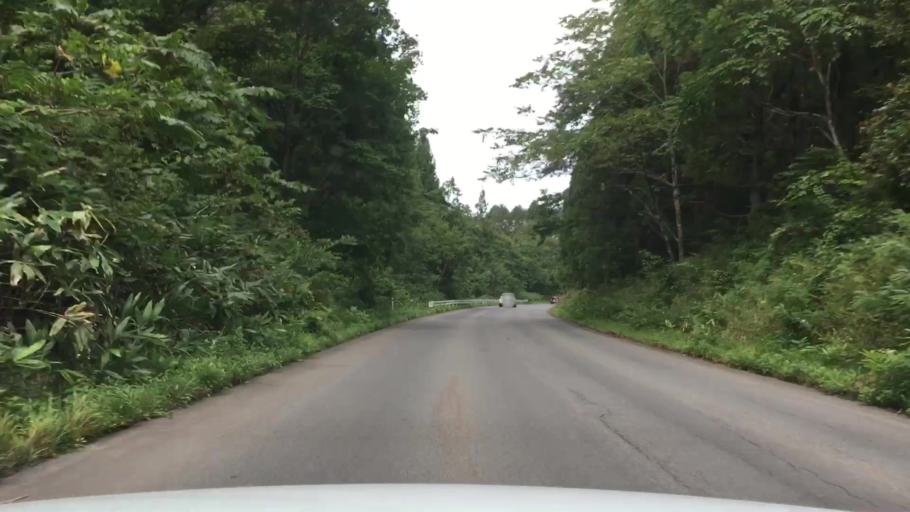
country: JP
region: Aomori
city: Shimokizukuri
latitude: 40.7167
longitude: 140.2601
